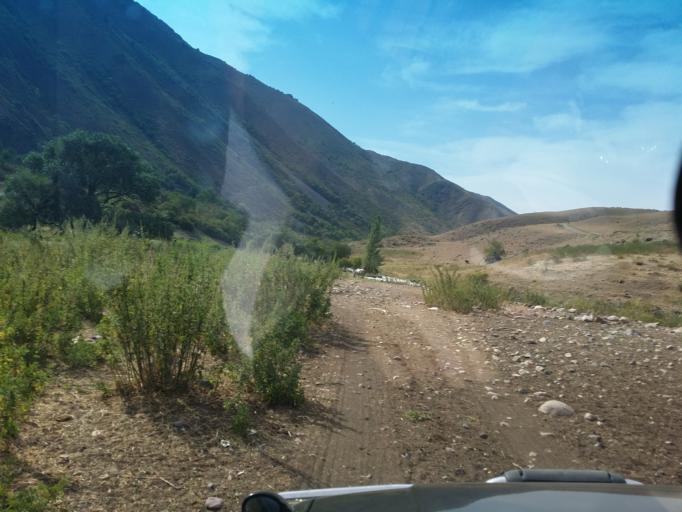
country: KZ
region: Almaty Oblysy
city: Turgen'
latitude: 43.2852
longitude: 77.6691
